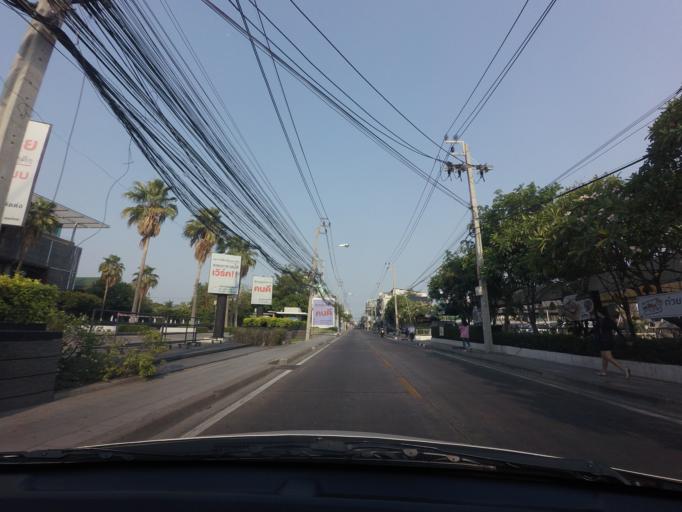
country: TH
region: Bangkok
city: Bang Na
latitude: 13.6620
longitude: 100.6033
